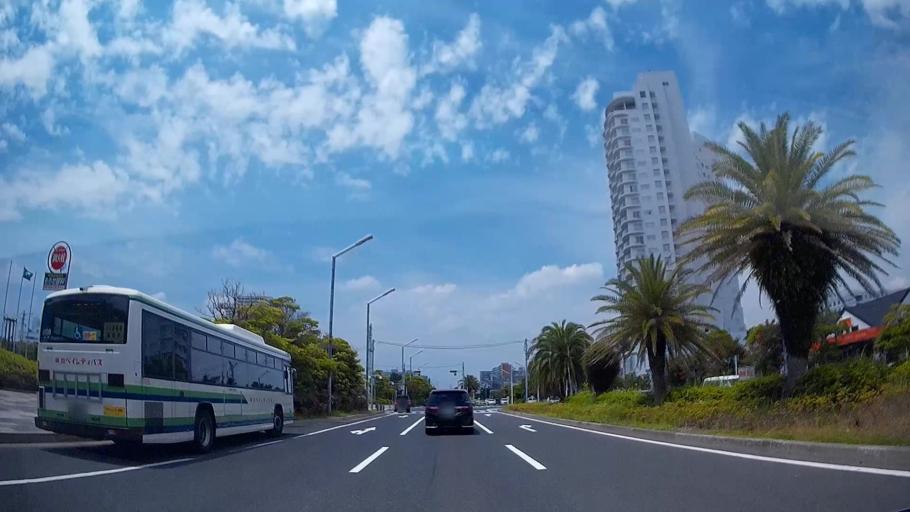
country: JP
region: Tokyo
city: Urayasu
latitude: 35.6459
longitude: 139.9204
